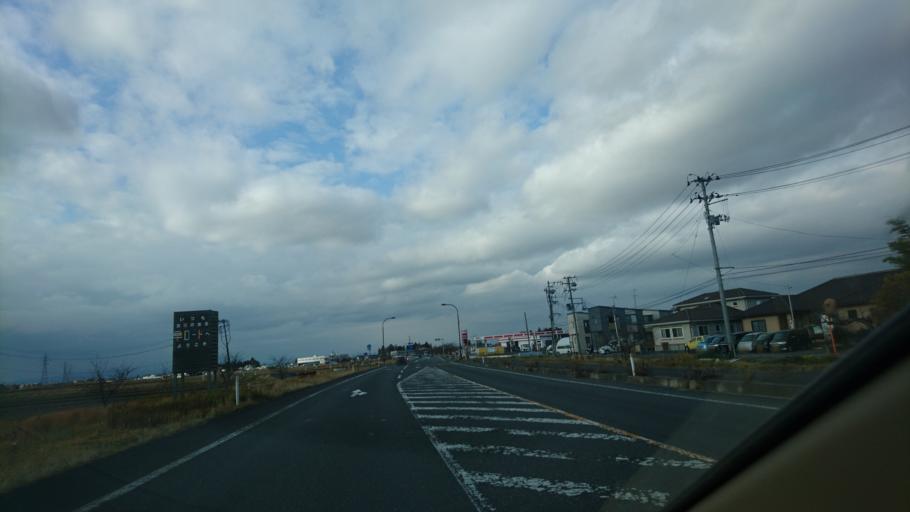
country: JP
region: Miyagi
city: Kogota
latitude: 38.5562
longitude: 141.0404
